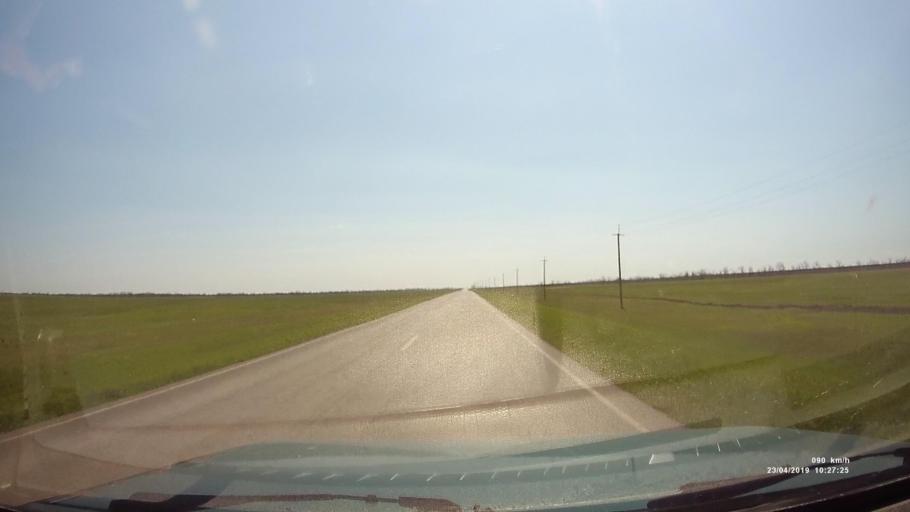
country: RU
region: Kalmykiya
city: Yashalta
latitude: 46.6140
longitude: 42.4907
